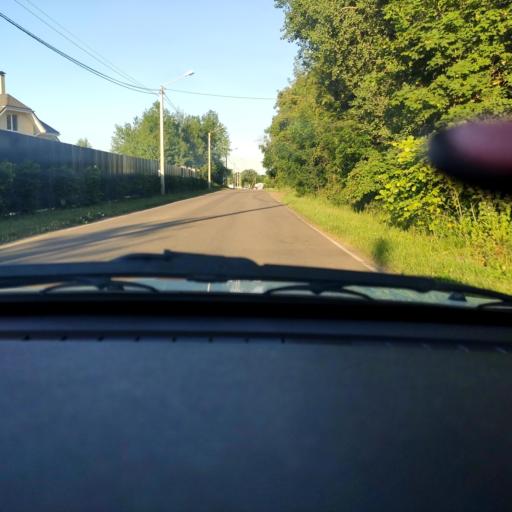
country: RU
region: Voronezj
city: Ramon'
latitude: 51.8902
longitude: 39.2662
